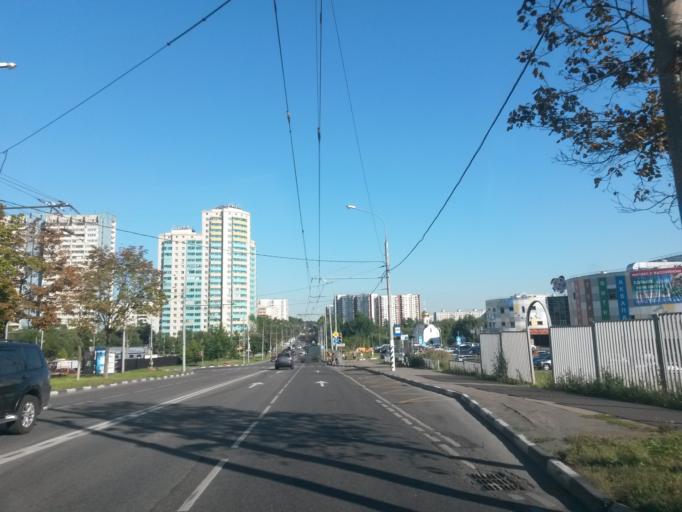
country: RU
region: Moscow
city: Yasenevo
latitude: 55.5989
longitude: 37.5260
